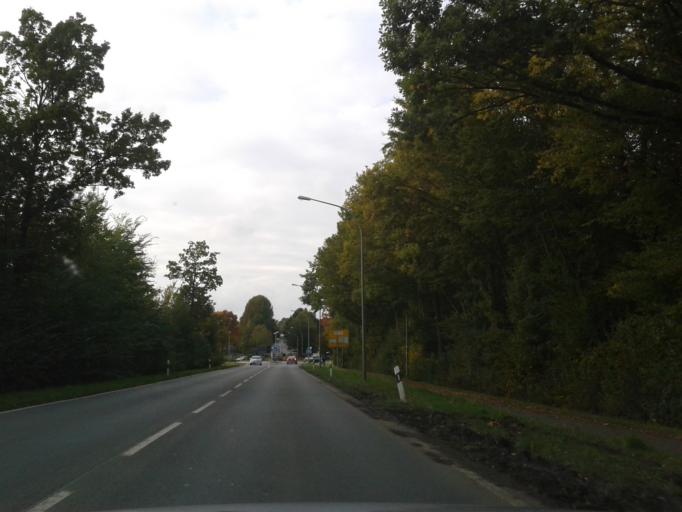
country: DE
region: North Rhine-Westphalia
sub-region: Regierungsbezirk Detmold
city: Bad Meinberg
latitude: 51.8933
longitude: 8.9774
